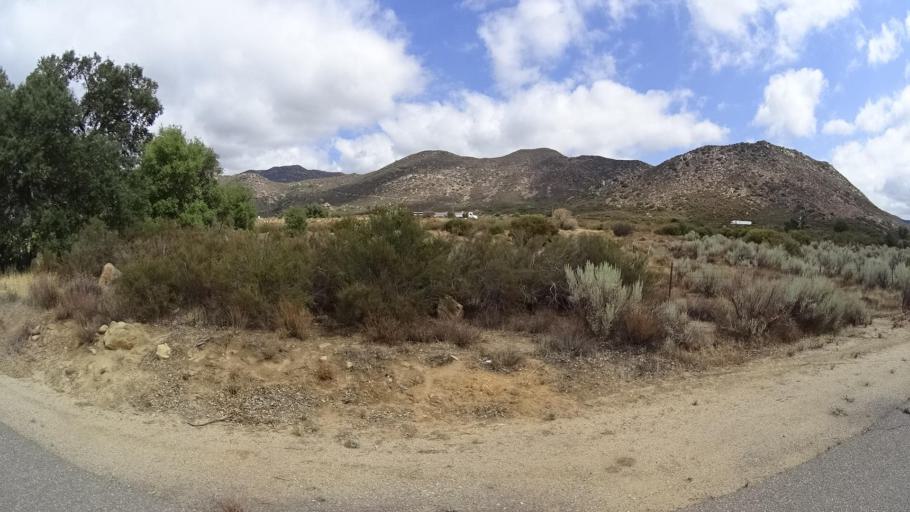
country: US
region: California
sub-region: San Diego County
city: Pine Valley
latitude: 32.7536
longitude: -116.4853
